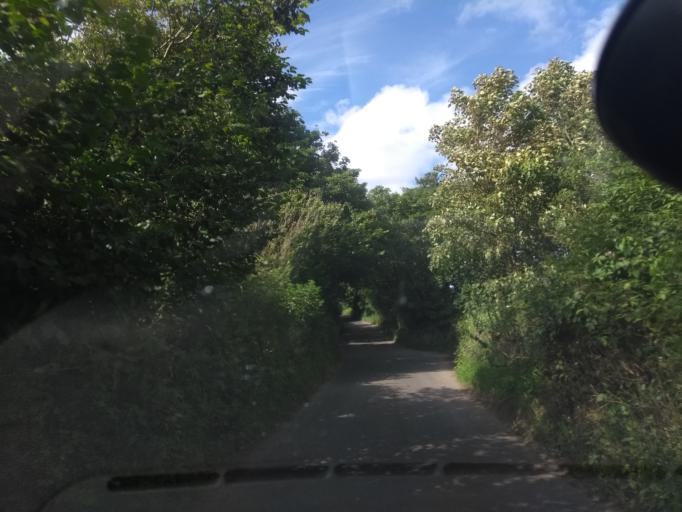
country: GB
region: England
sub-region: Devon
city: Modbury
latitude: 50.3048
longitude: -3.8858
